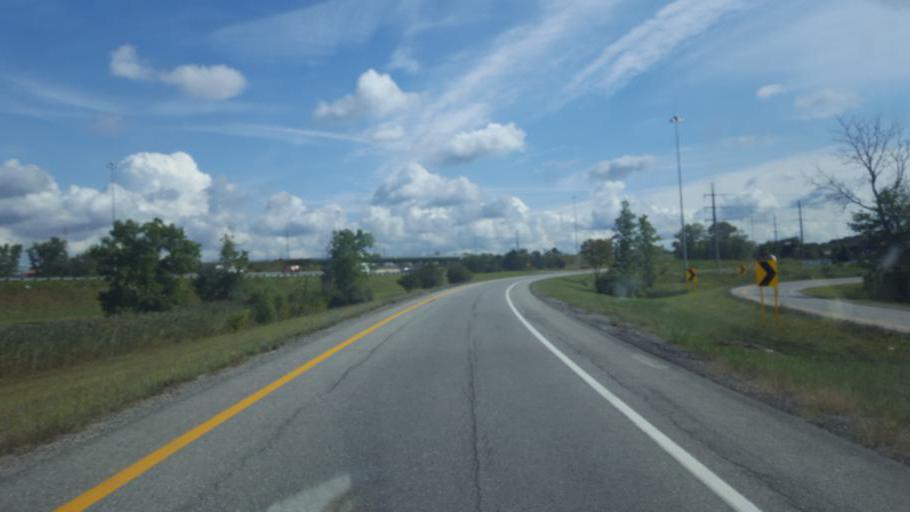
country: US
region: Ohio
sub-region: Cuyahoga County
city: North Randall
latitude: 41.4281
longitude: -81.5054
